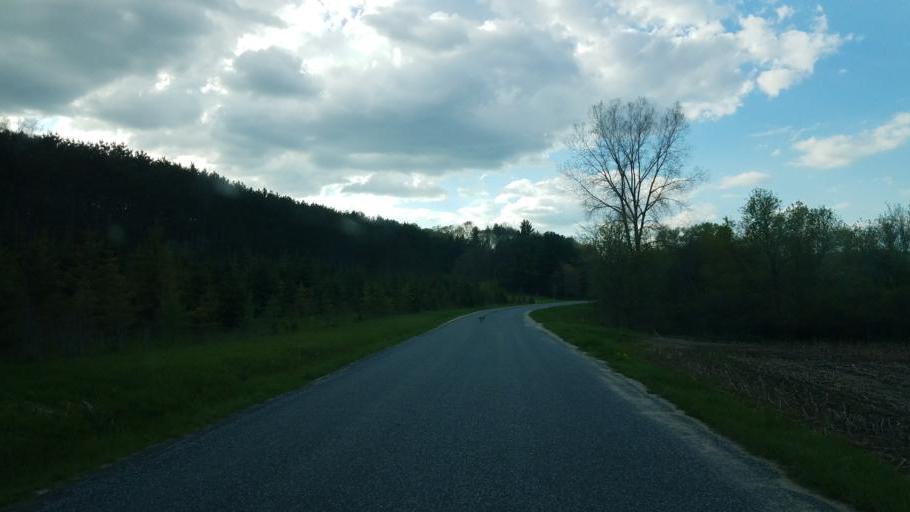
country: US
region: Wisconsin
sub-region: Vernon County
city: Hillsboro
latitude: 43.6693
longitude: -90.3889
